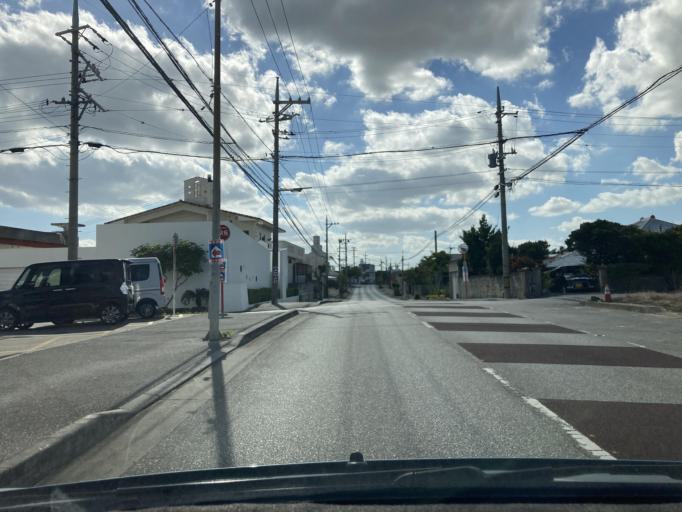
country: JP
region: Okinawa
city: Gushikawa
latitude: 26.3437
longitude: 127.8484
